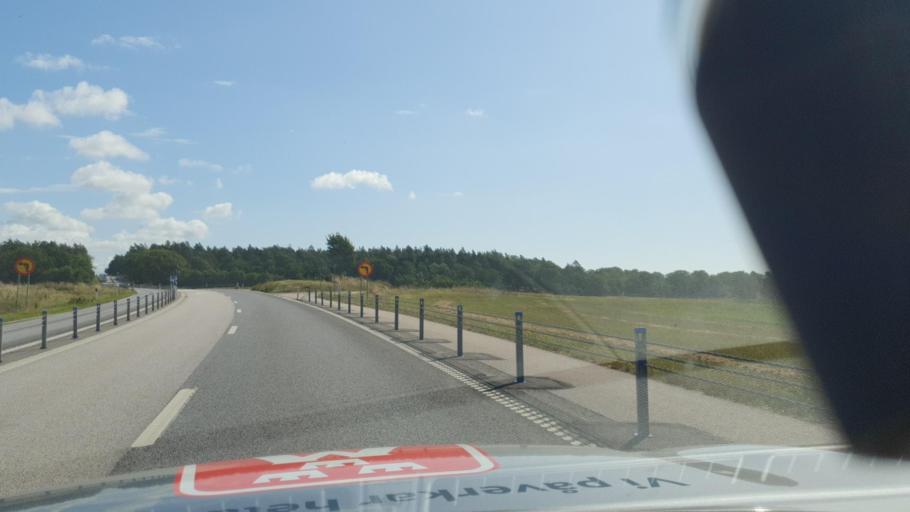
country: SE
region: Blekinge
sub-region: Karlskrona Kommun
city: Nattraby
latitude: 56.1976
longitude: 15.4459
